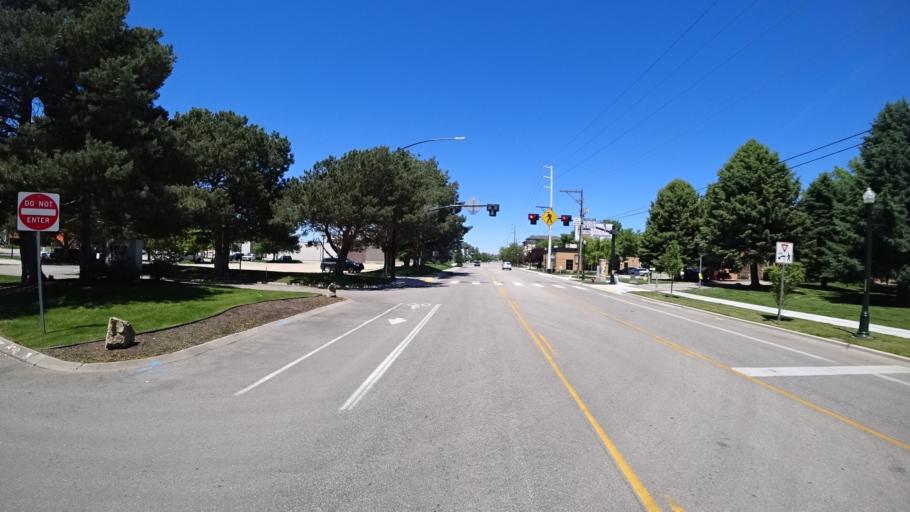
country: US
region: Idaho
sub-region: Ada County
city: Boise
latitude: 43.6133
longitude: -116.2135
